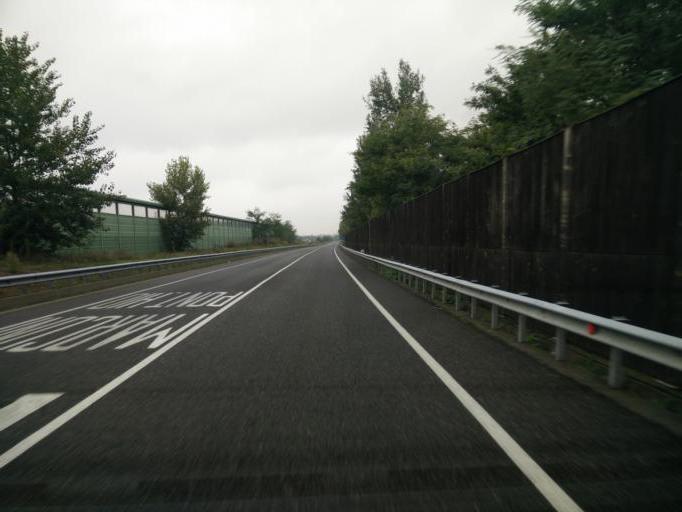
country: IT
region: Emilia-Romagna
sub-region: Provincia di Bologna
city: Borgonuovo
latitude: 44.4350
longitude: 11.2775
